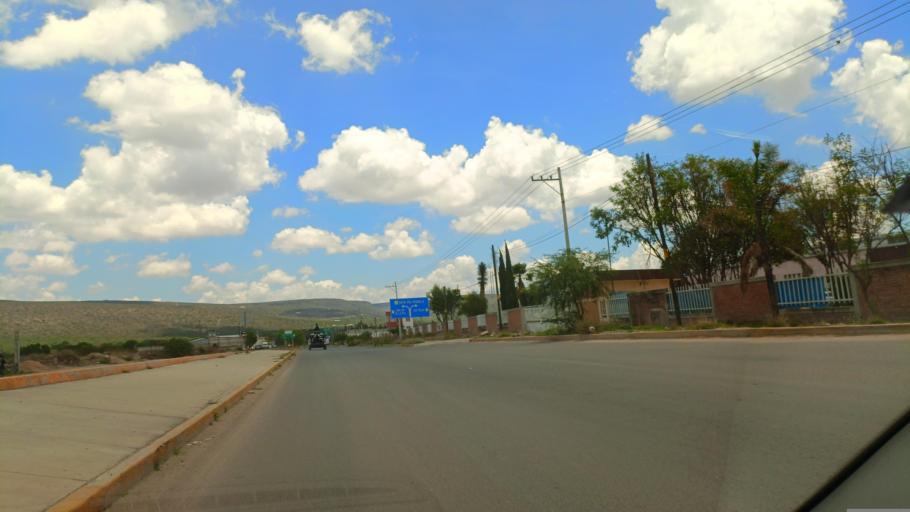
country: MX
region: Guanajuato
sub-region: San Luis de la Paz
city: San Luis de la Paz
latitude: 21.2907
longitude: -100.4909
